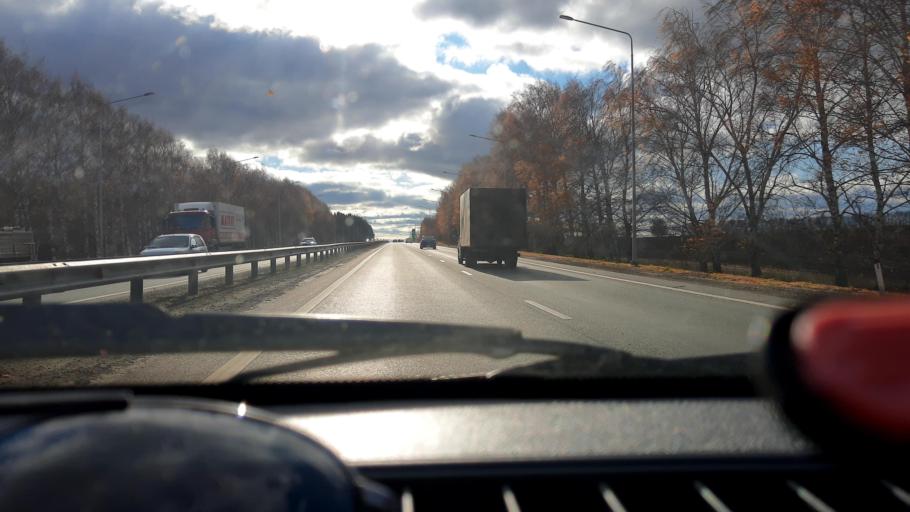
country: RU
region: Bashkortostan
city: Ufa
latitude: 54.5310
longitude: 55.9040
